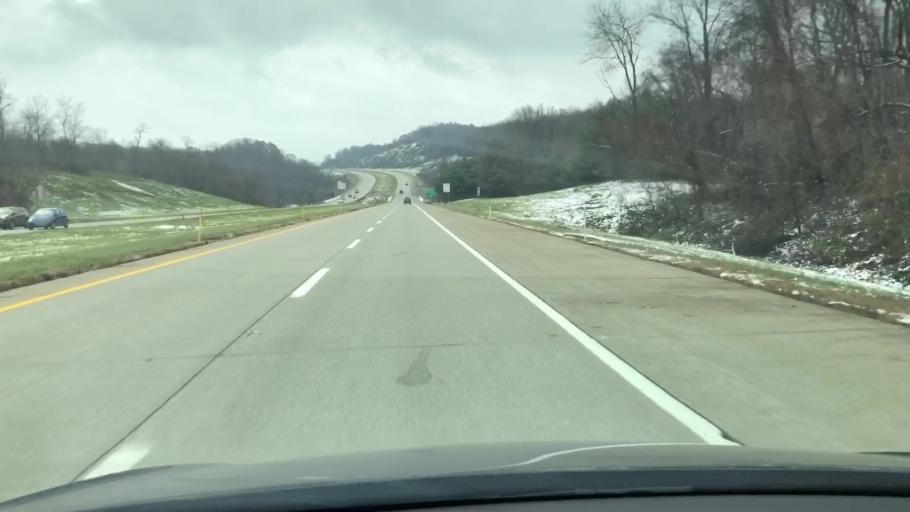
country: US
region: Pennsylvania
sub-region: Westmoreland County
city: New Stanton
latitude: 40.2614
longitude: -79.6135
